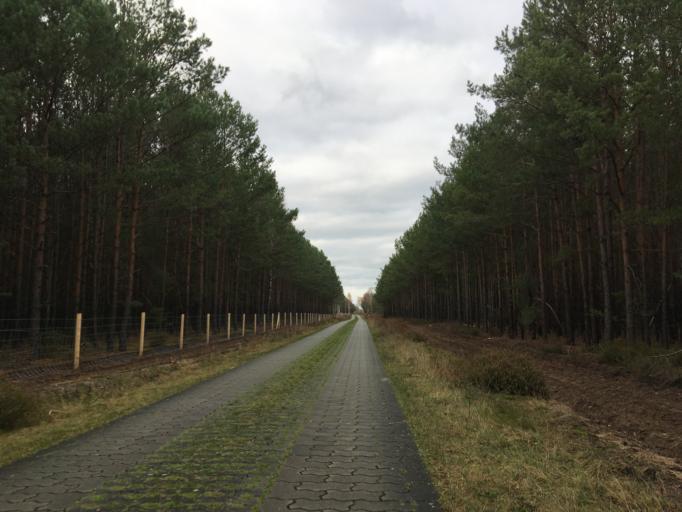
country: DE
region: Brandenburg
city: Tauer
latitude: 51.9972
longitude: 14.5114
